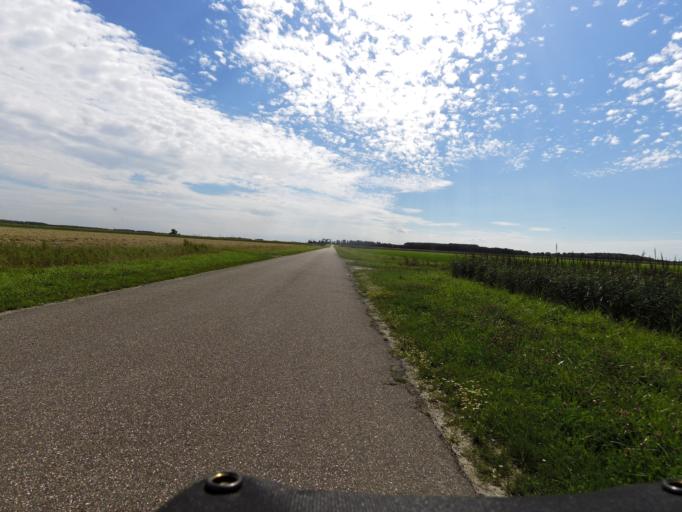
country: NL
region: Zeeland
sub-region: Gemeente Noord-Beveland
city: Kamperland
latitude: 51.5443
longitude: 3.7192
